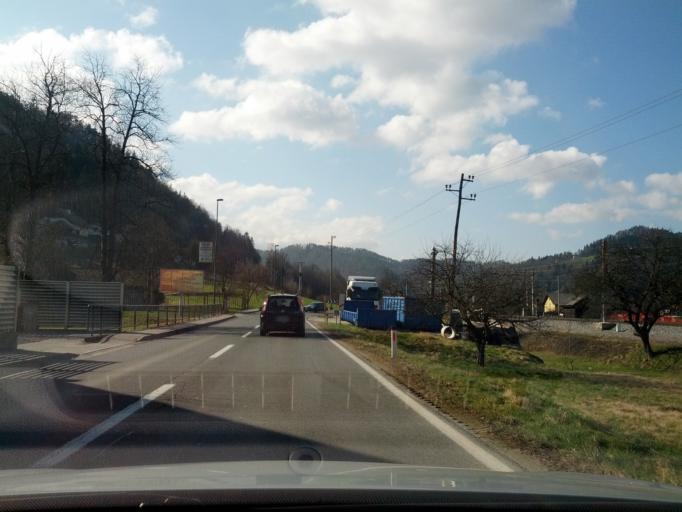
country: SI
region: Litija
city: Litija
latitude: 46.0762
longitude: 14.8248
